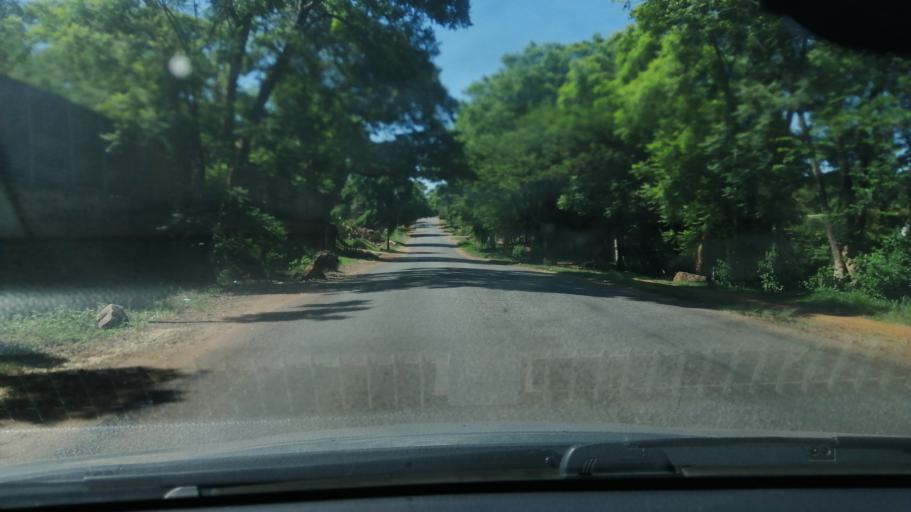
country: ZW
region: Harare
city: Harare
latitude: -17.7979
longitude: 31.1286
